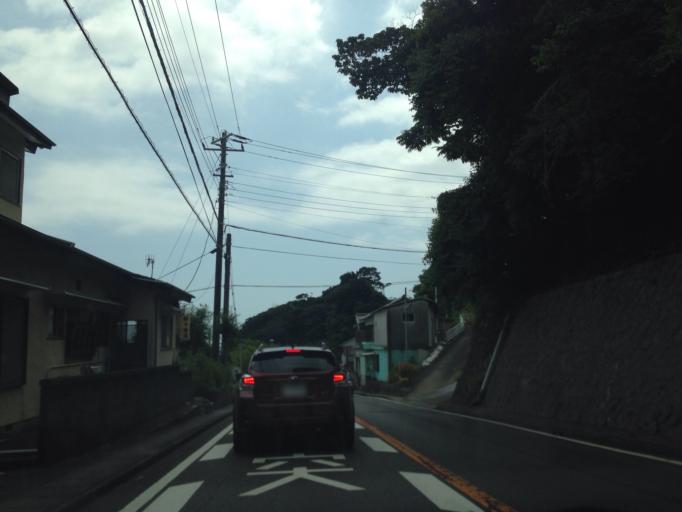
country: JP
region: Shizuoka
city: Shimoda
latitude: 34.7098
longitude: 138.9784
